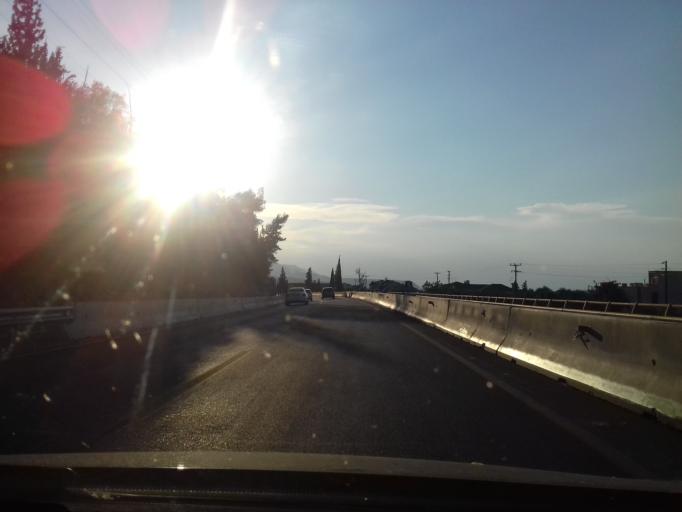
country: GR
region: West Greece
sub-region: Nomos Achaias
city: Aiyira
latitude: 38.1335
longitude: 22.4335
